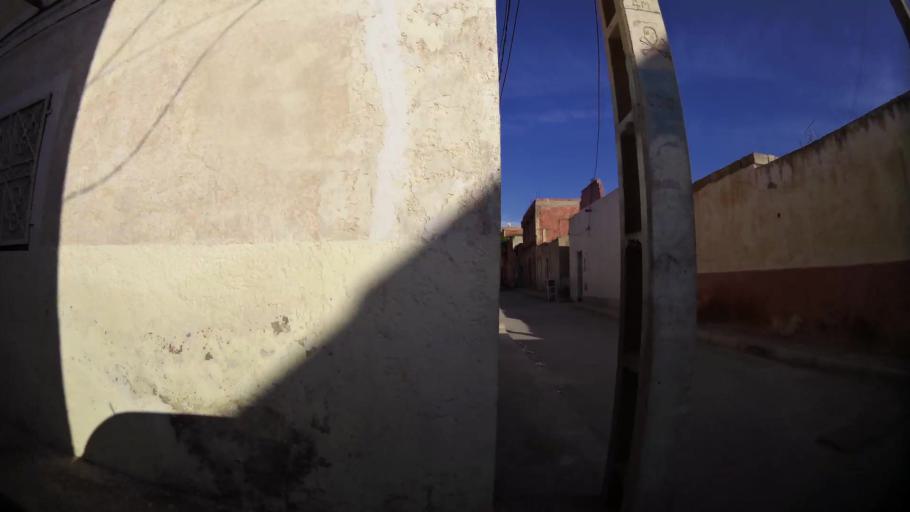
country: MA
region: Oriental
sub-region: Oujda-Angad
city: Oujda
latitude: 34.7120
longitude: -1.9031
